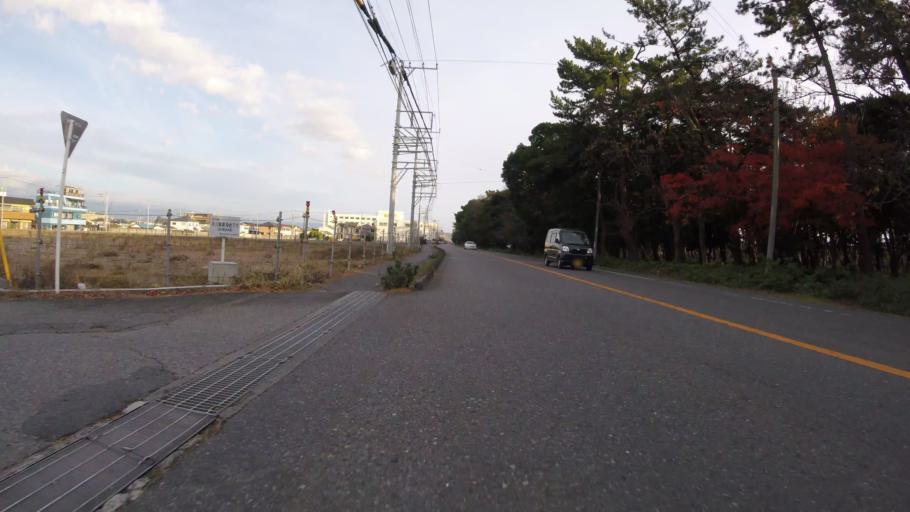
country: JP
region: Shizuoka
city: Numazu
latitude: 35.1184
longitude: 138.8085
